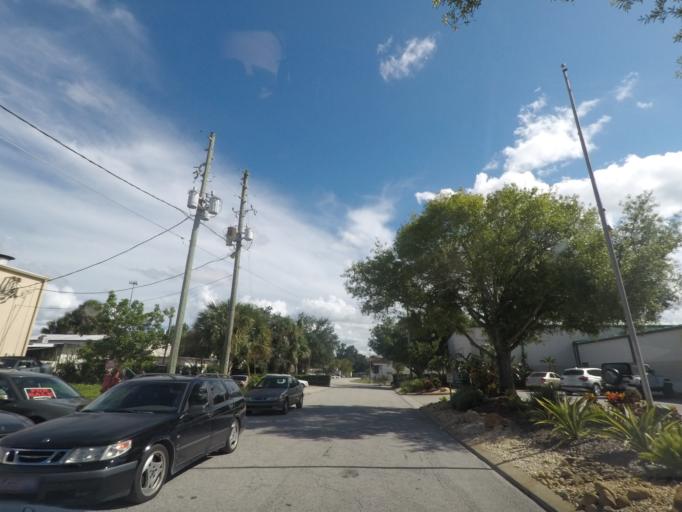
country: US
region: Florida
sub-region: Orange County
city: Fairview Shores
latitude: 28.5917
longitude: -81.3708
